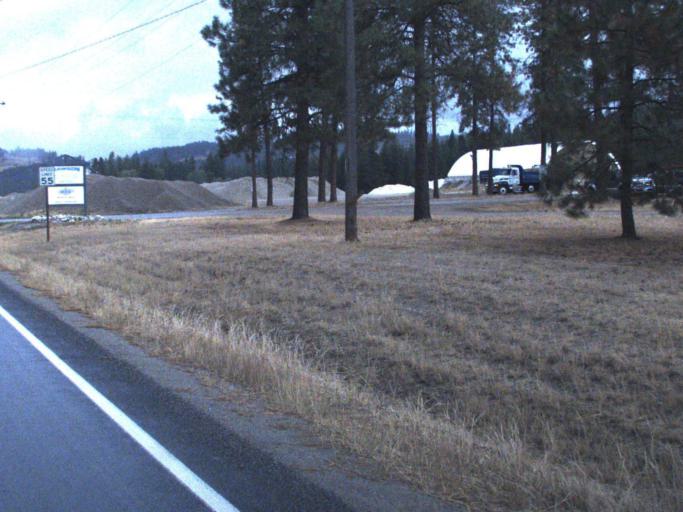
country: US
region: Washington
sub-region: Stevens County
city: Chewelah
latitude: 48.1568
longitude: -117.7258
